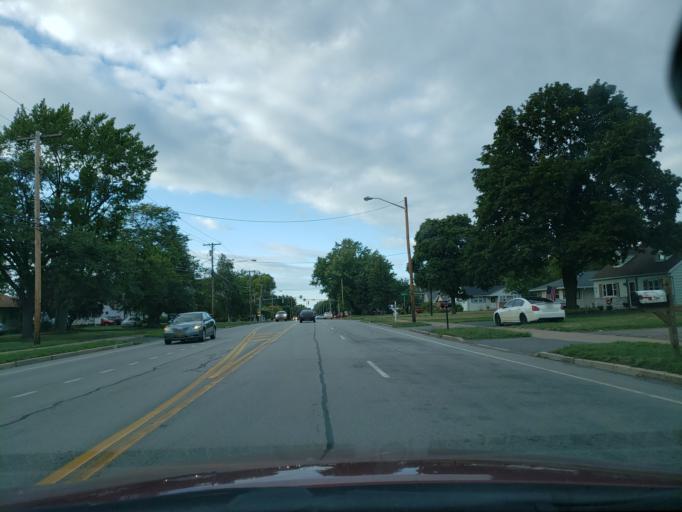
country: US
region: New York
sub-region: Monroe County
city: Greece
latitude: 43.2369
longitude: -77.6591
